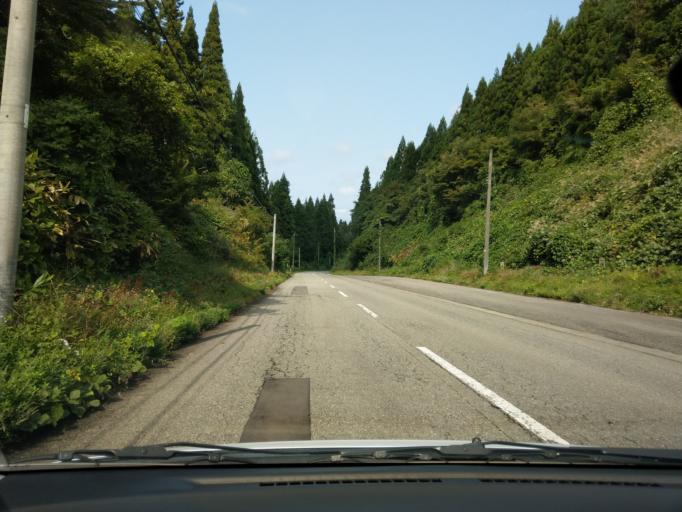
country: JP
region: Akita
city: Omagari
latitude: 39.5120
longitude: 140.3076
